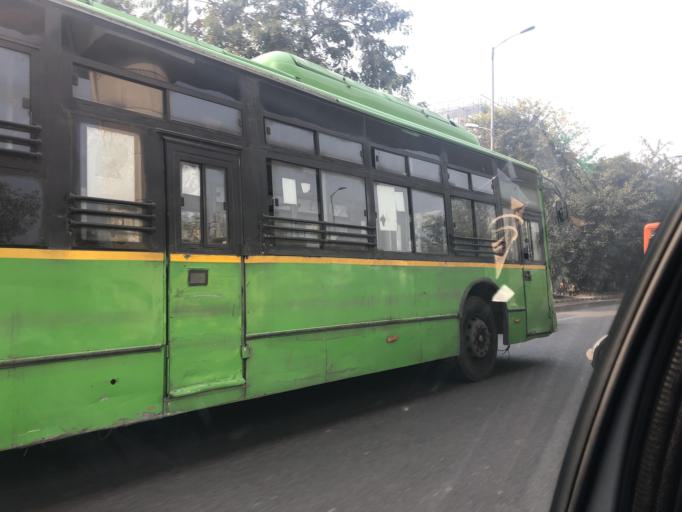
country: IN
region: NCT
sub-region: North West Delhi
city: Pitampura
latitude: 28.6753
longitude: 77.1276
